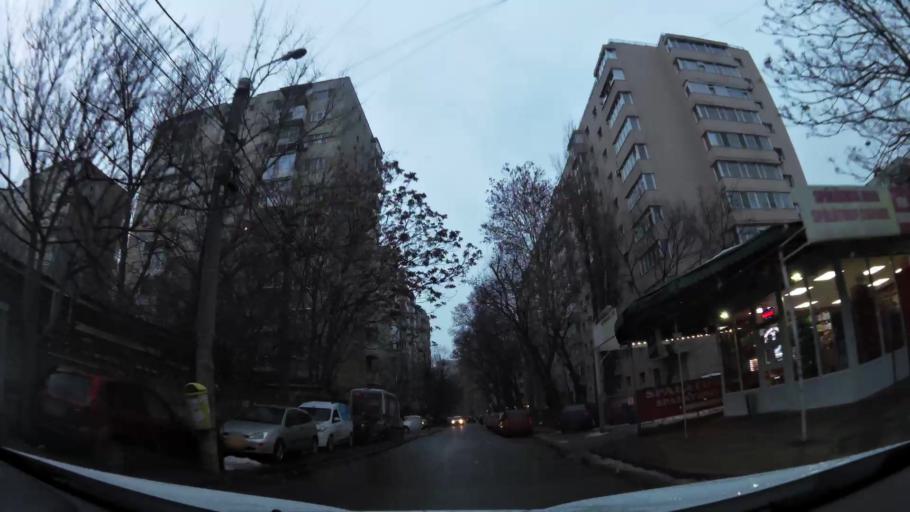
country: RO
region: Ilfov
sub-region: Comuna Chiajna
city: Rosu
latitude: 44.4317
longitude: 26.0237
